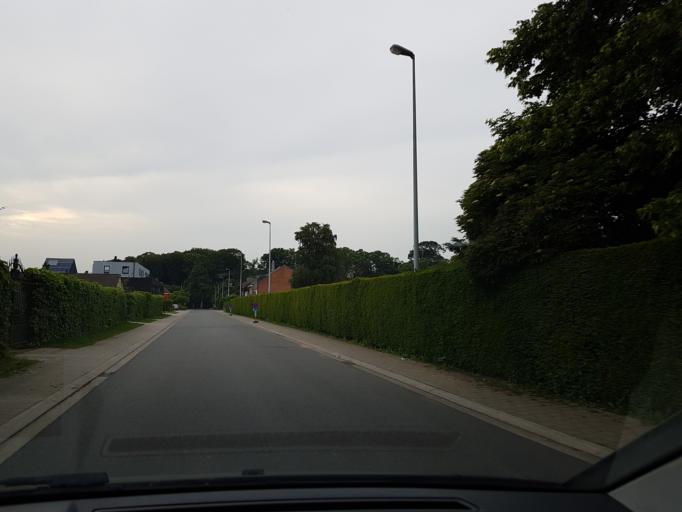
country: BE
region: Flanders
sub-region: Provincie Oost-Vlaanderen
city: Dendermonde
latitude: 50.9792
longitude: 4.0854
